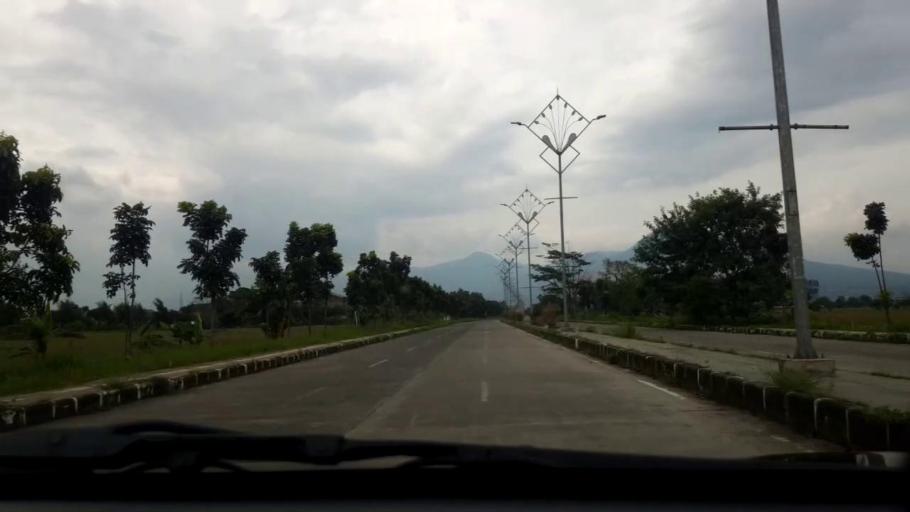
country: ID
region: West Java
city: Cileunyi
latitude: -6.9642
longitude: 107.7095
